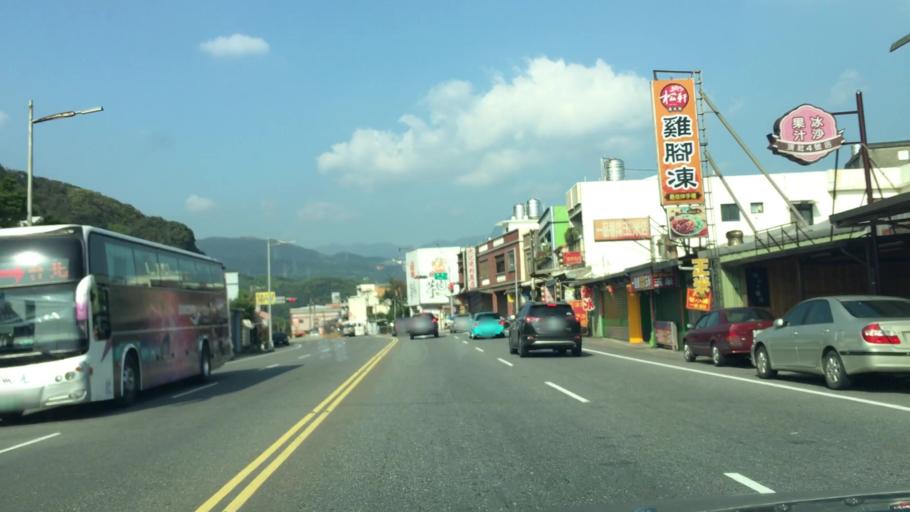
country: TW
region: Taiwan
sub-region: Keelung
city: Keelung
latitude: 25.2096
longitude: 121.6569
